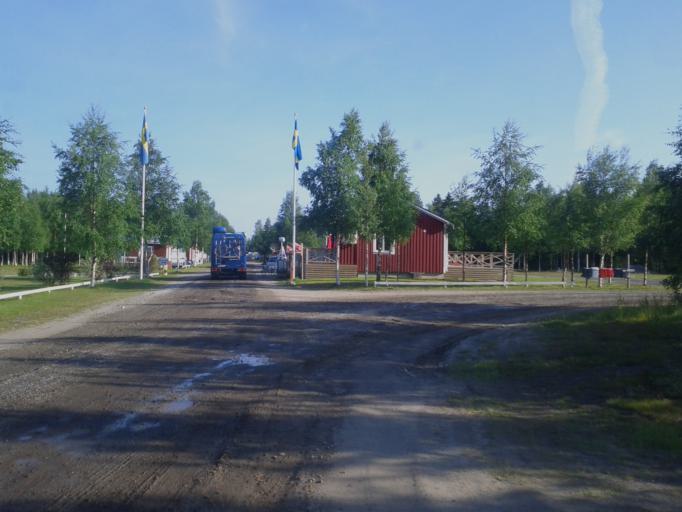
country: SE
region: Vaesterbotten
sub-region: Robertsfors Kommun
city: Robertsfors
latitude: 64.1574
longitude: 20.9736
